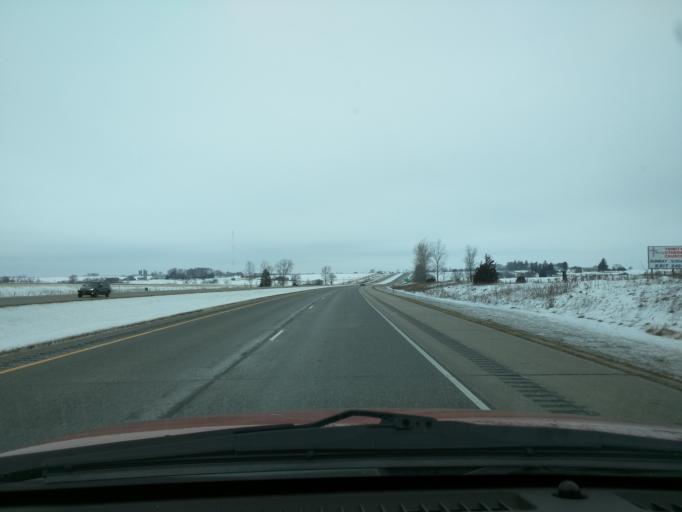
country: US
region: Minnesota
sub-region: Winona County
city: Goodview
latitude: 43.9479
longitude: -91.7091
